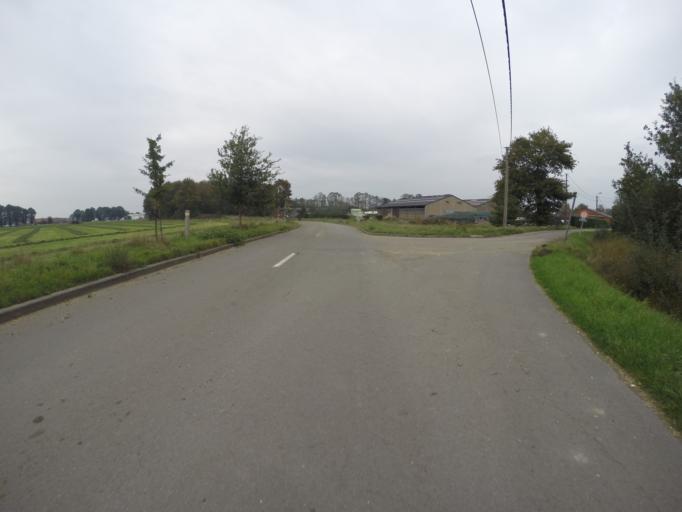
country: BE
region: Flanders
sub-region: Provincie West-Vlaanderen
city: Beernem
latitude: 51.1178
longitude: 3.3516
